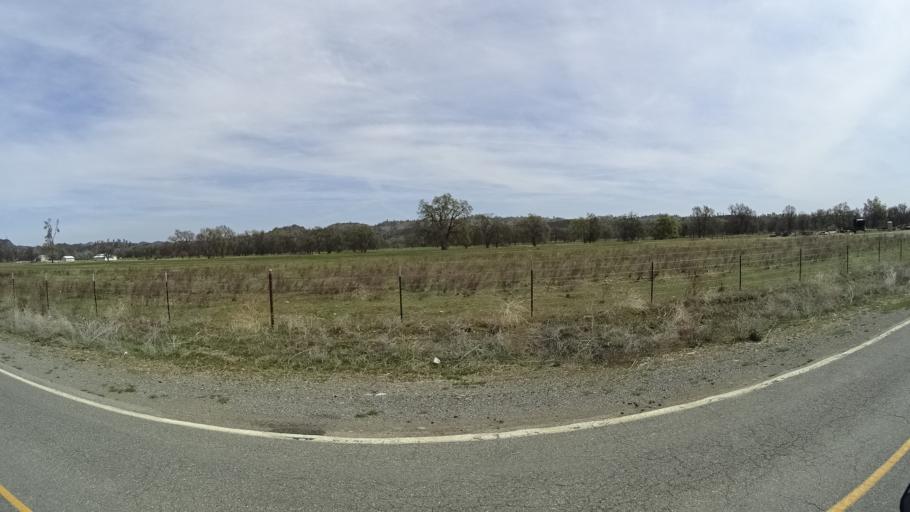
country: US
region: California
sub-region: Glenn County
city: Willows
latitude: 39.4018
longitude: -122.5523
